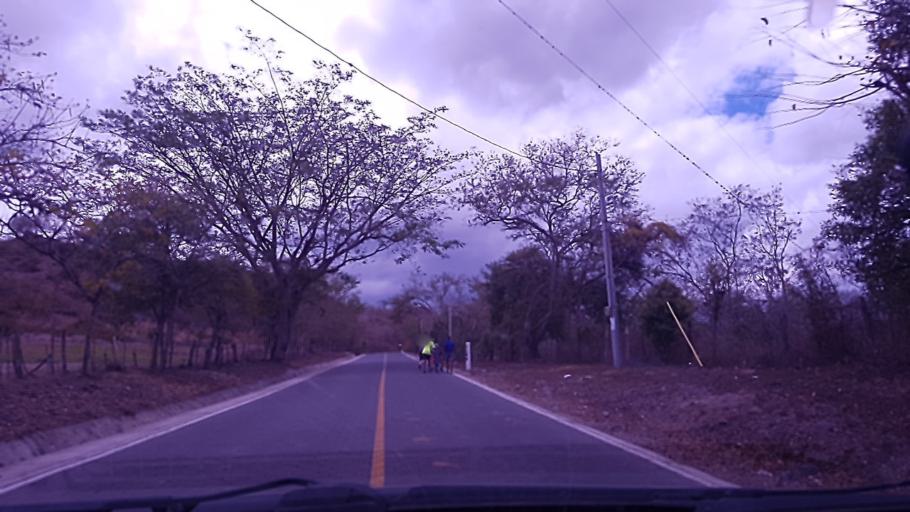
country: NI
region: Esteli
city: Condega
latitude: 13.3734
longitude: -86.3845
